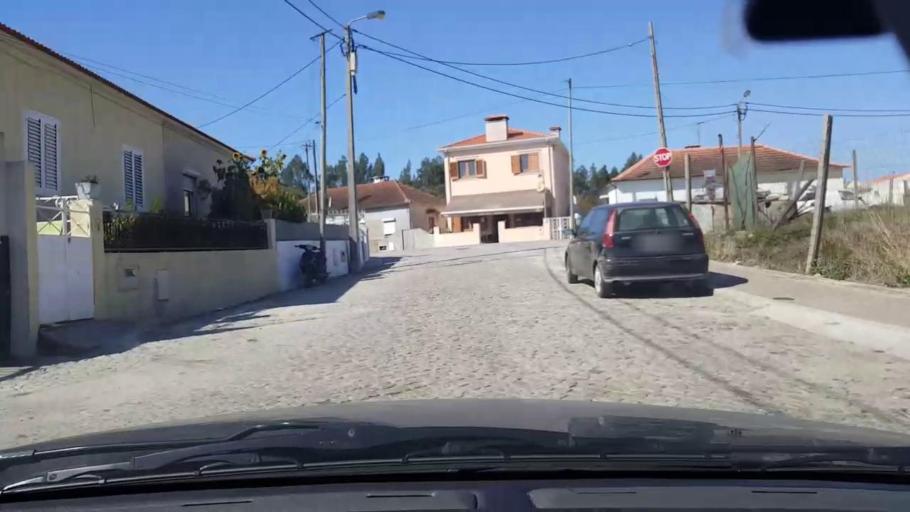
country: PT
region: Porto
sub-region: Matosinhos
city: Lavra
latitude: 41.2938
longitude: -8.6986
